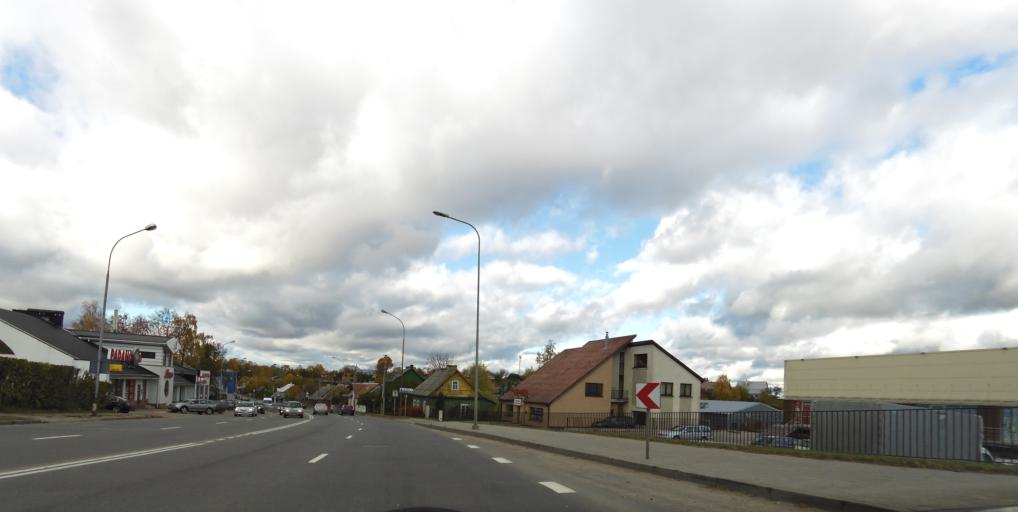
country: LT
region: Vilnius County
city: Rasos
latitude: 54.6606
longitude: 25.3034
